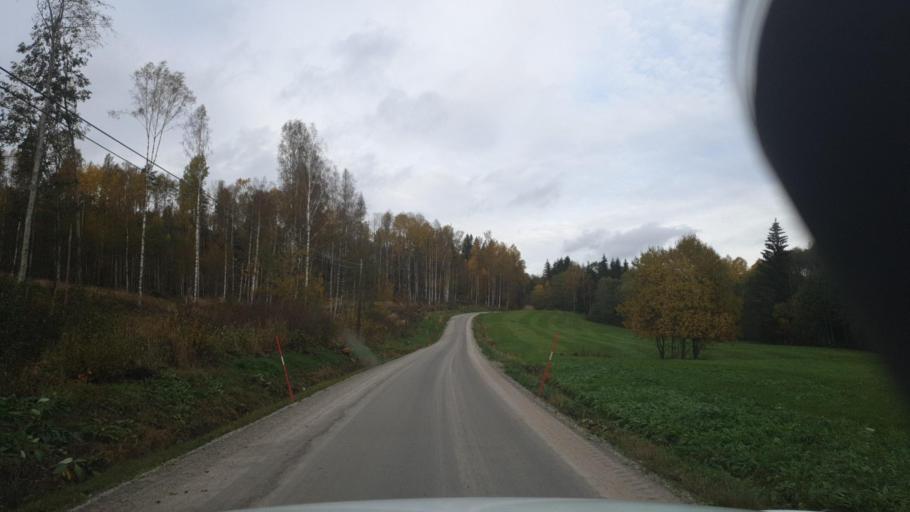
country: SE
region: Vaermland
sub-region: Sunne Kommun
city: Sunne
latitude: 59.6945
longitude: 12.8863
